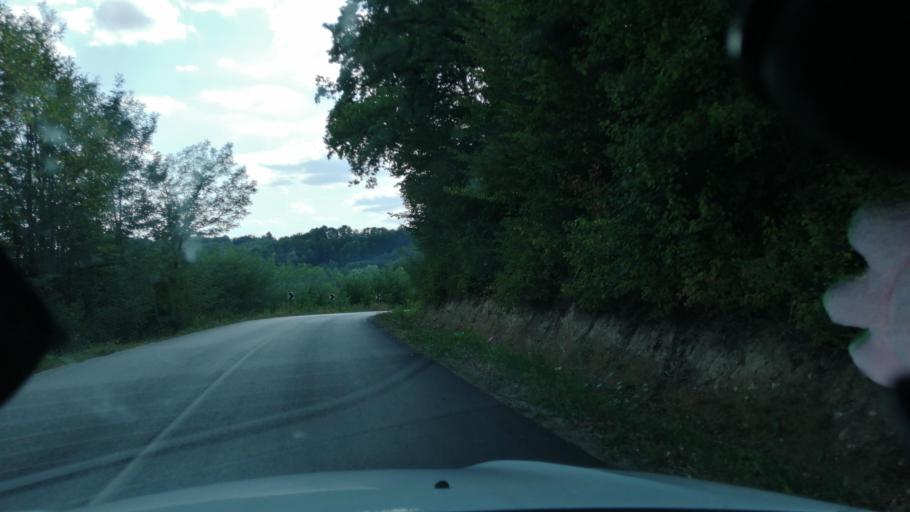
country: RS
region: Central Serbia
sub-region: Moravicki Okrug
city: Cacak
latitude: 43.8011
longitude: 20.2653
